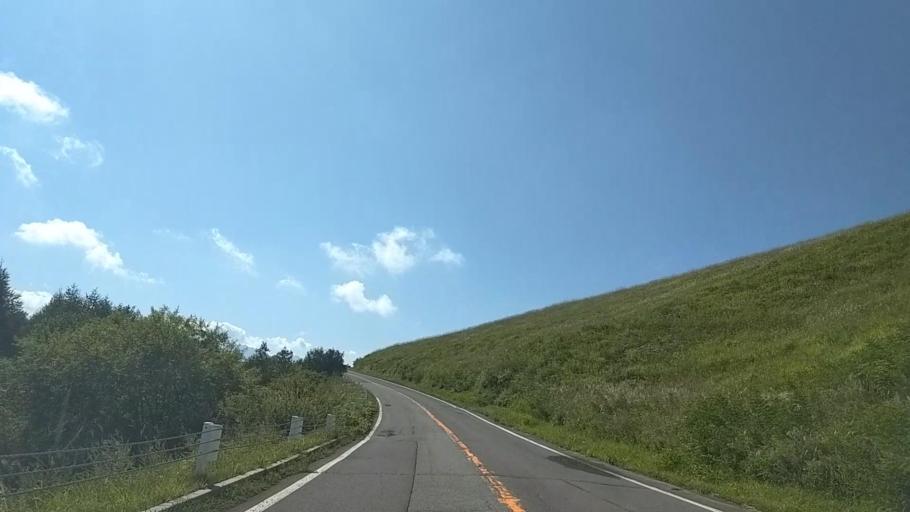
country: JP
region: Nagano
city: Suwa
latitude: 36.0999
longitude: 138.2187
